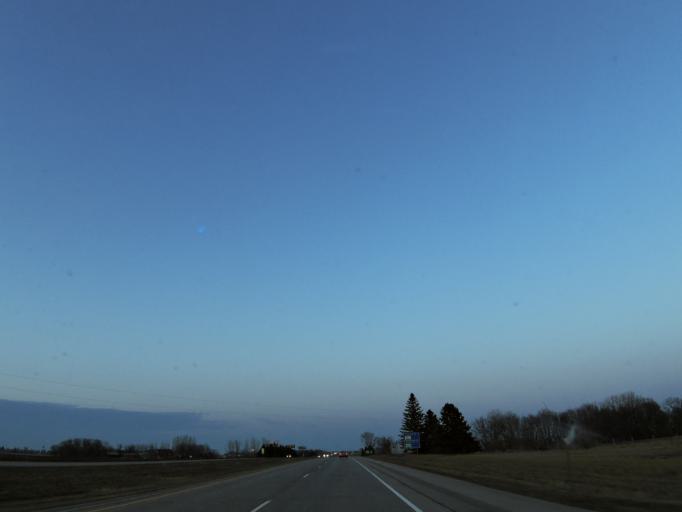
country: US
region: Minnesota
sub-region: Mower County
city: Grand Meadow
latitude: 43.7021
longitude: -92.7130
